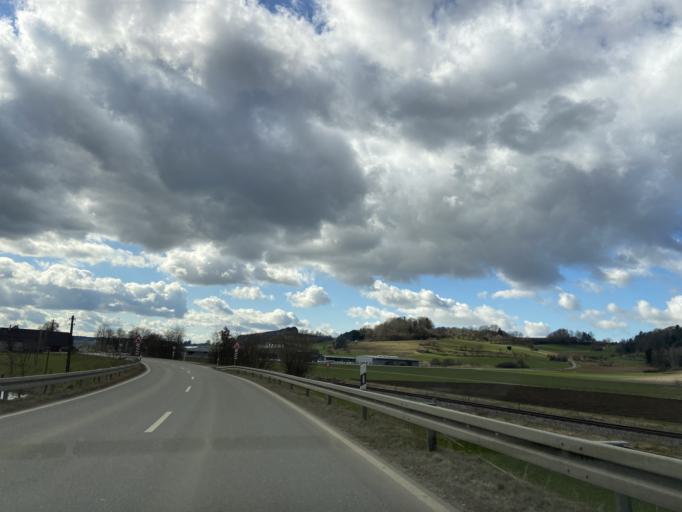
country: DE
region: Baden-Wuerttemberg
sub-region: Tuebingen Region
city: Krauchenwies
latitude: 48.0097
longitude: 9.2041
